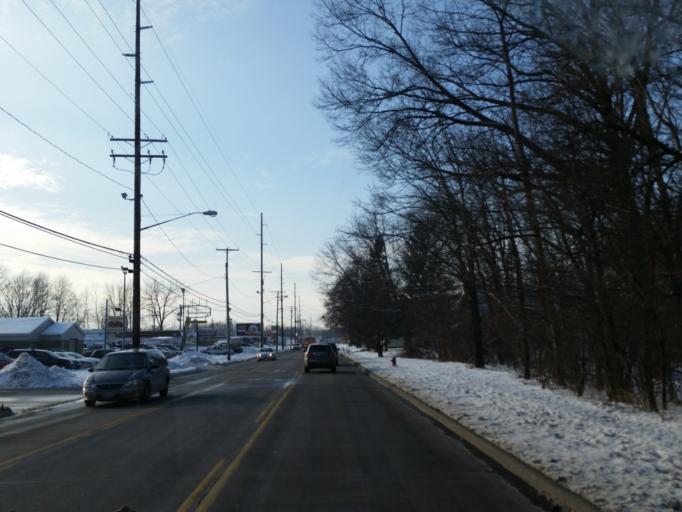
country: US
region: Ohio
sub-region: Lorain County
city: Lorain
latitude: 41.4655
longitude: -82.1517
